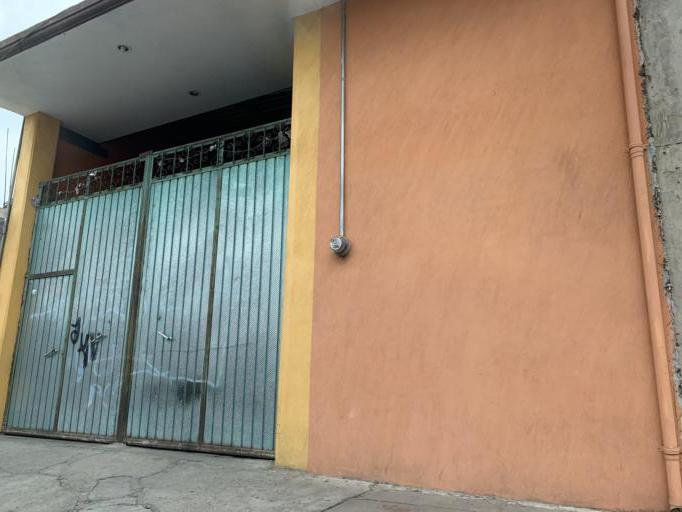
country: MX
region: Puebla
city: Huejotzingo
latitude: 19.1624
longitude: -98.4068
